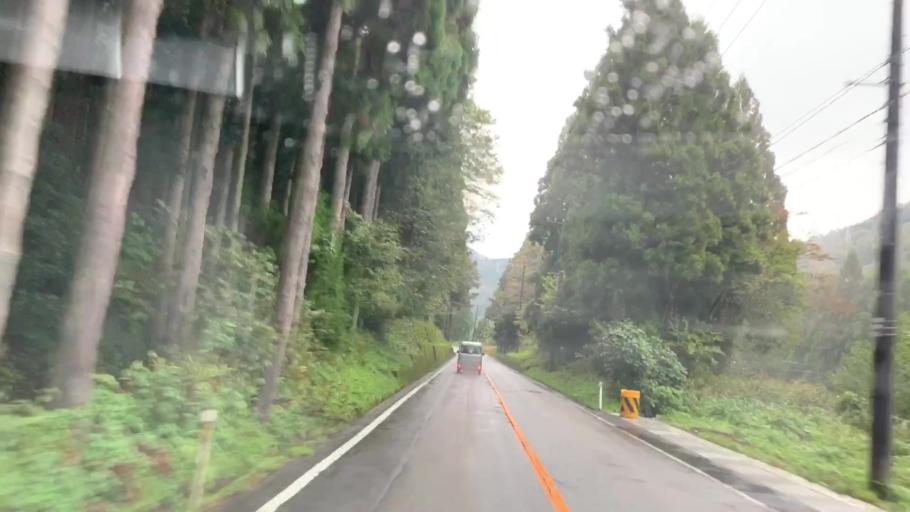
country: JP
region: Toyama
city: Kamiichi
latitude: 36.5785
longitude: 137.3406
